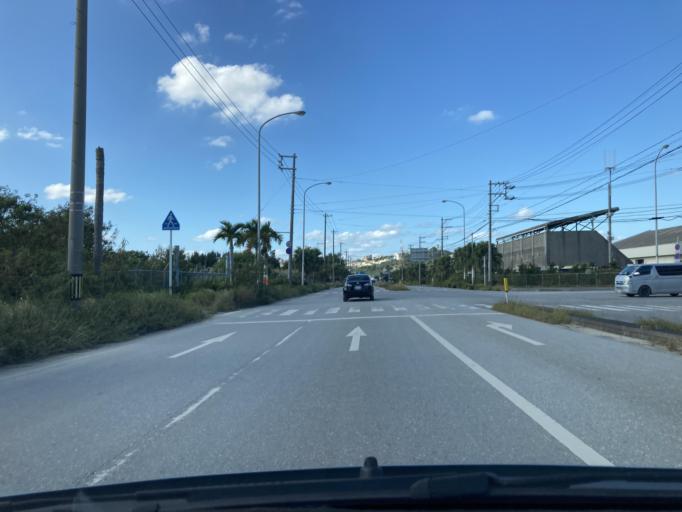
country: JP
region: Okinawa
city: Katsuren-haebaru
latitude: 26.3290
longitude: 127.8426
